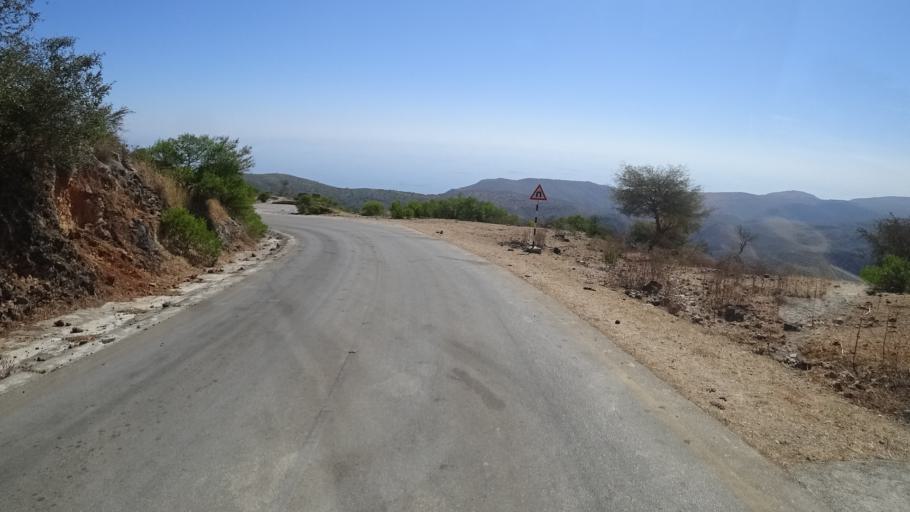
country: YE
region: Al Mahrah
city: Hawf
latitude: 16.7677
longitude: 53.3370
